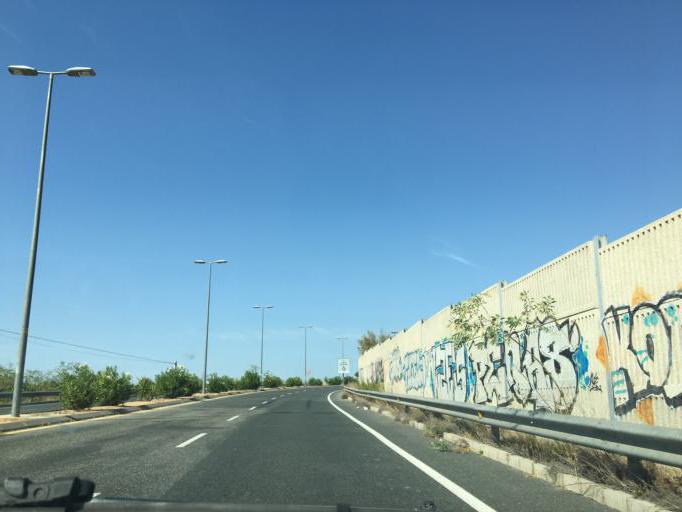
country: ES
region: Murcia
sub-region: Murcia
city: Murcia
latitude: 38.0440
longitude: -1.1348
